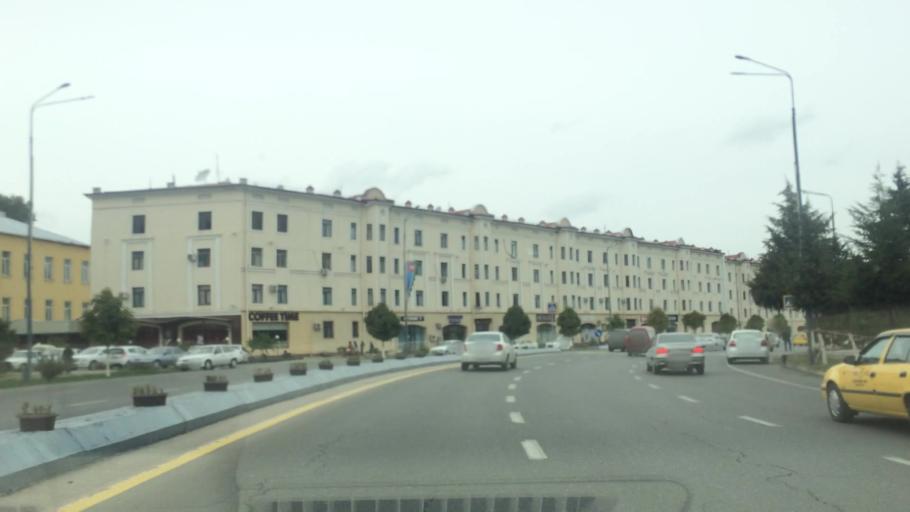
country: UZ
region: Samarqand
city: Samarqand
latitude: 39.6520
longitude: 66.9626
